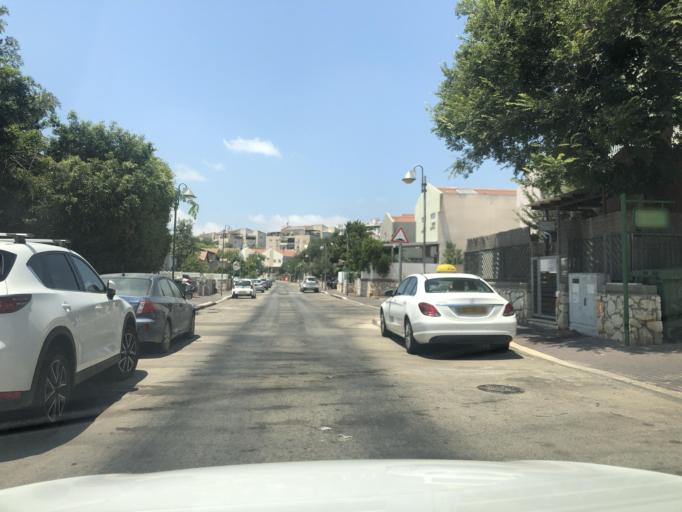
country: IL
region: Haifa
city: Daliyat el Karmil
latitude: 32.6358
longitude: 35.0913
